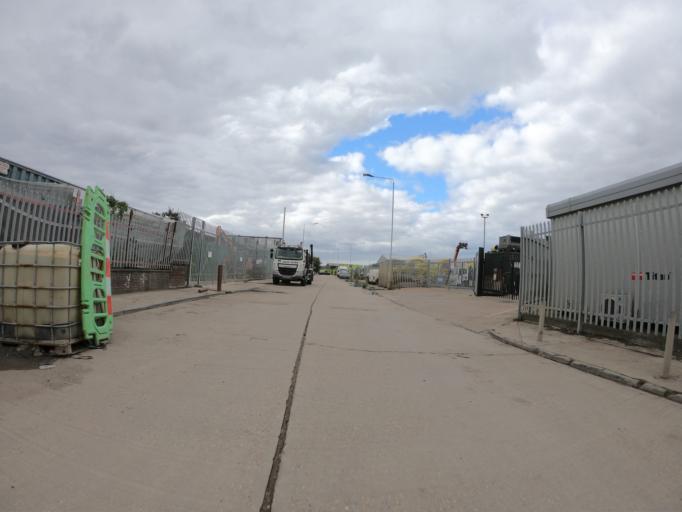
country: GB
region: England
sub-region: Essex
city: Purfleet
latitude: 51.4780
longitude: 0.2126
